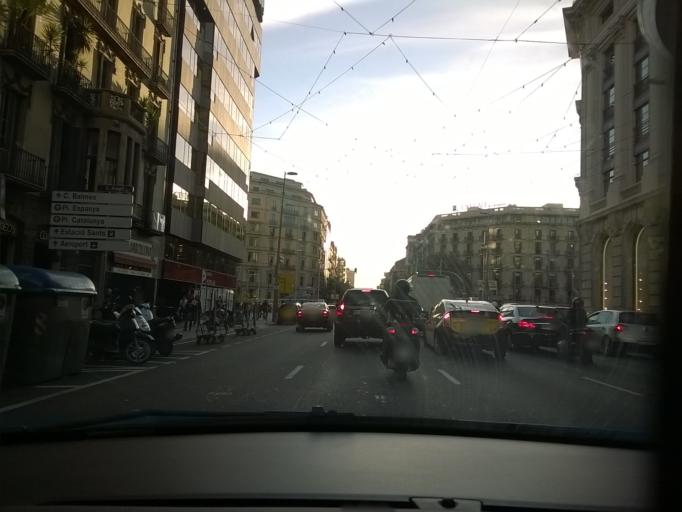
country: ES
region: Catalonia
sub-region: Provincia de Barcelona
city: Eixample
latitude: 41.3928
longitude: 2.1658
